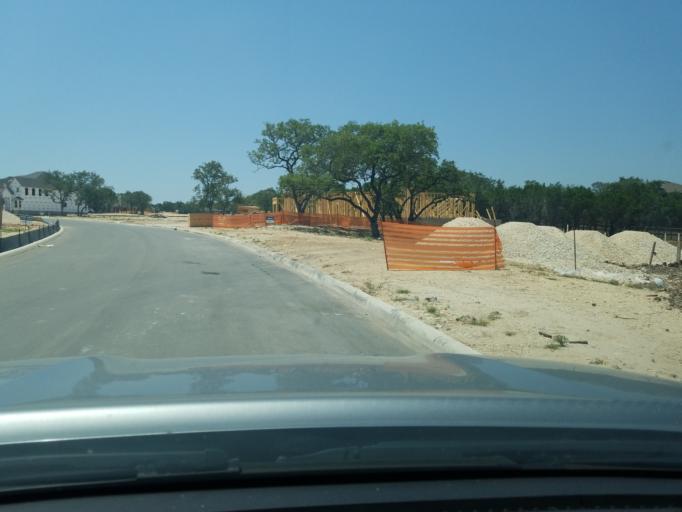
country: US
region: Texas
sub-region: Bexar County
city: Timberwood Park
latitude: 29.7152
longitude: -98.5069
